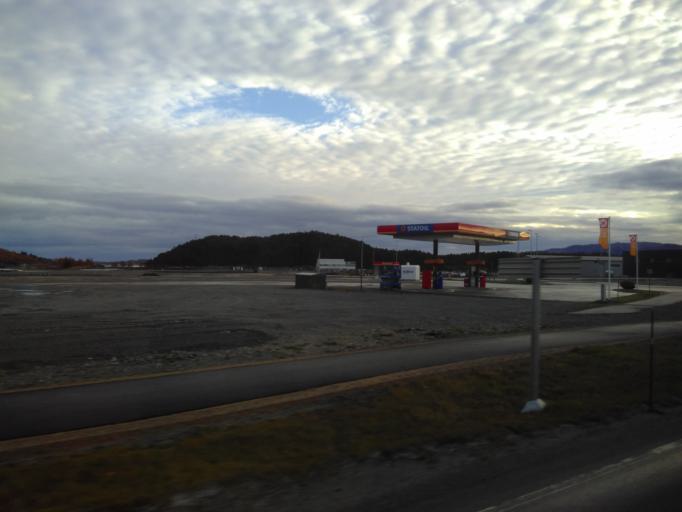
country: NO
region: Sor-Trondelag
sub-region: Hitra
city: Fillan
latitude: 63.5213
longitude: 9.1067
